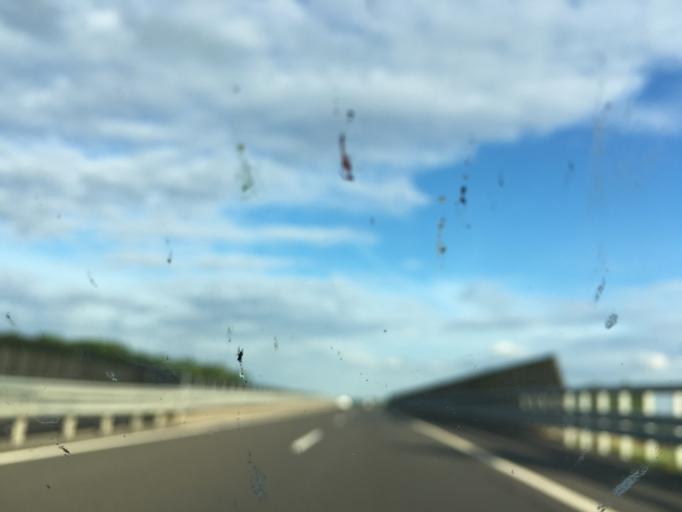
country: HU
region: Hajdu-Bihar
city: Balmazujvaros
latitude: 47.7360
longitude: 21.3682
